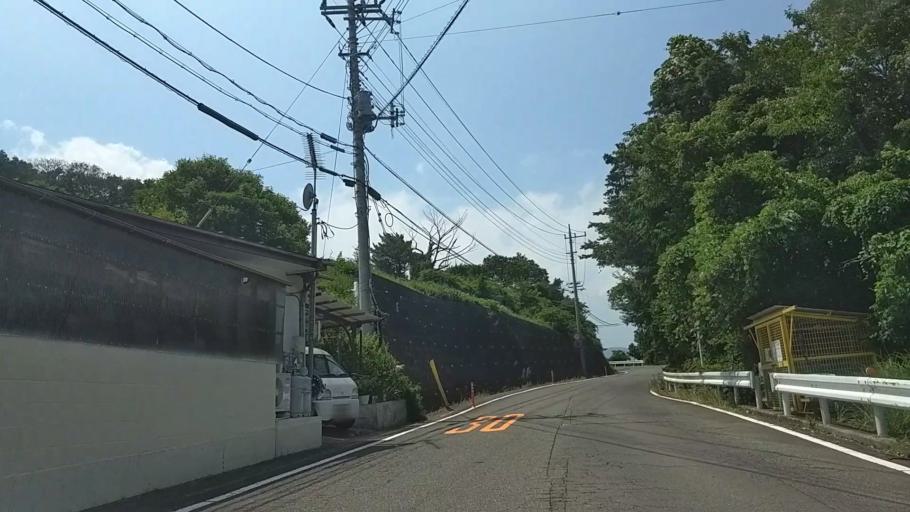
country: JP
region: Shizuoka
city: Ito
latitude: 34.9444
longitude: 139.1134
